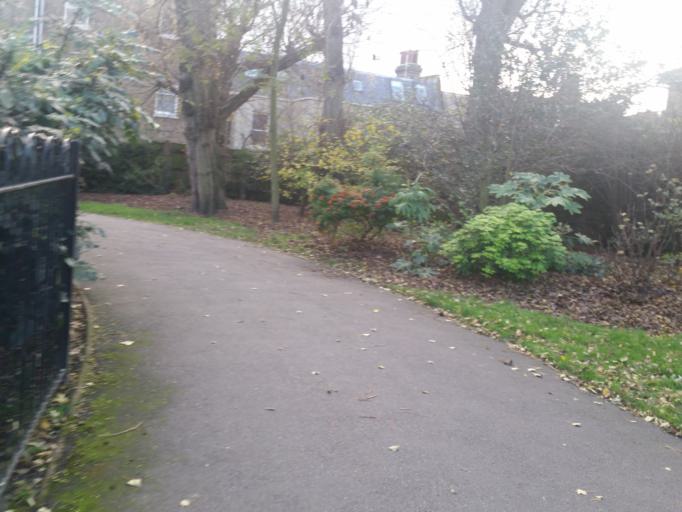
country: GB
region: England
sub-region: Greater London
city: Hammersmith
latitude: 51.5095
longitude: -0.2286
